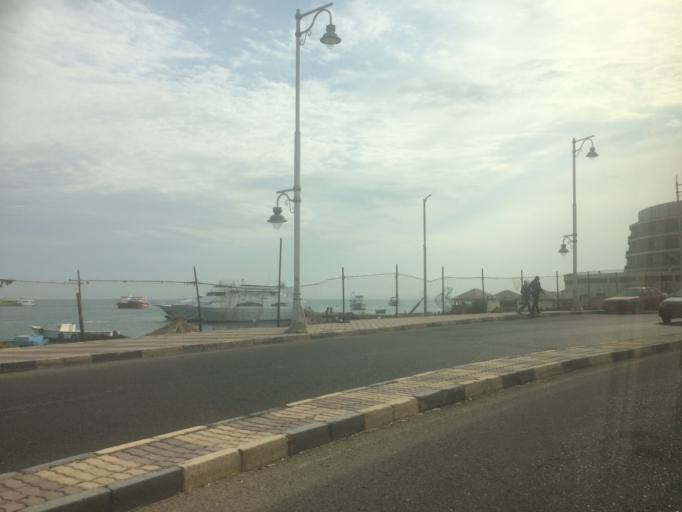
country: EG
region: Red Sea
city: Hurghada
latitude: 27.1987
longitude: 33.8497
